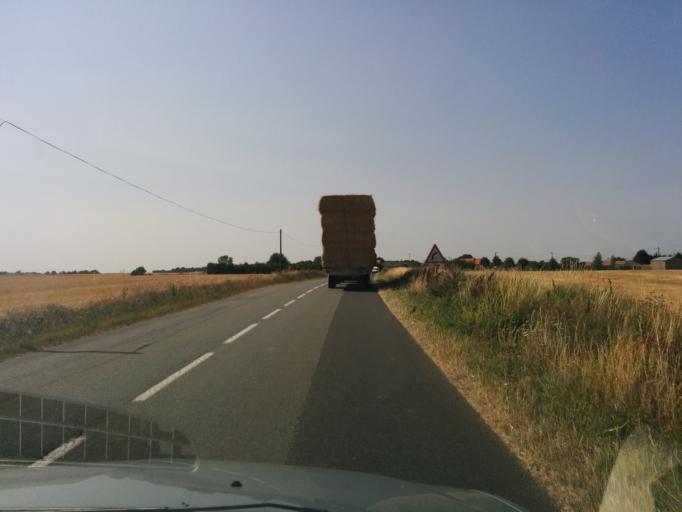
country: FR
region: Poitou-Charentes
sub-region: Departement de la Vienne
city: Mirebeau
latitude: 46.7429
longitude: 0.1802
